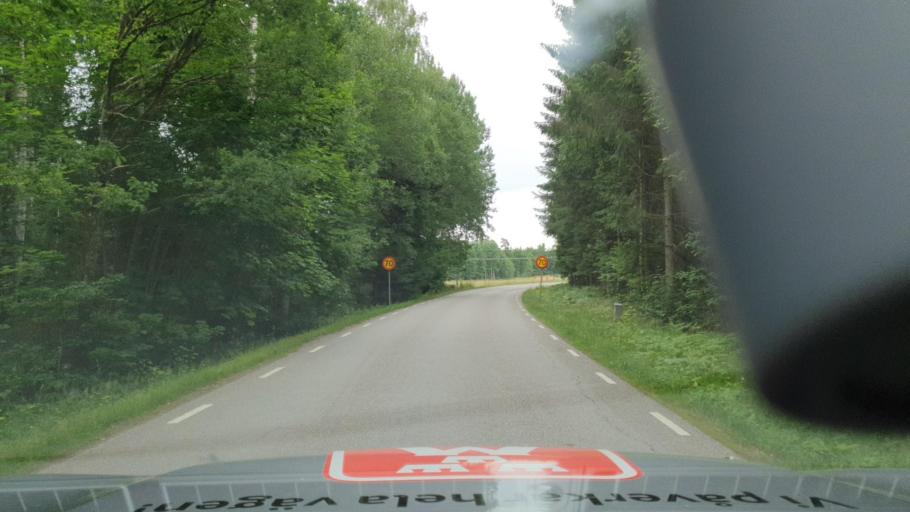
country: SE
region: Kalmar
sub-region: Kalmar Kommun
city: Trekanten
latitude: 56.6162
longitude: 16.0567
